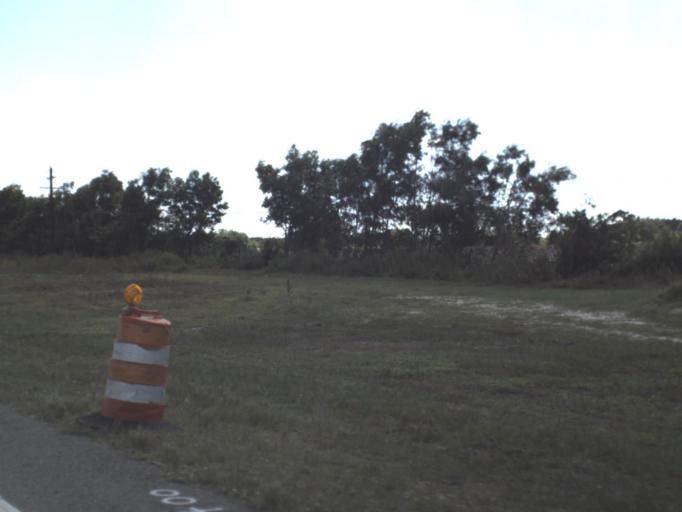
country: US
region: Florida
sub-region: Collier County
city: Lely Resort
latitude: 26.0316
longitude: -81.6496
